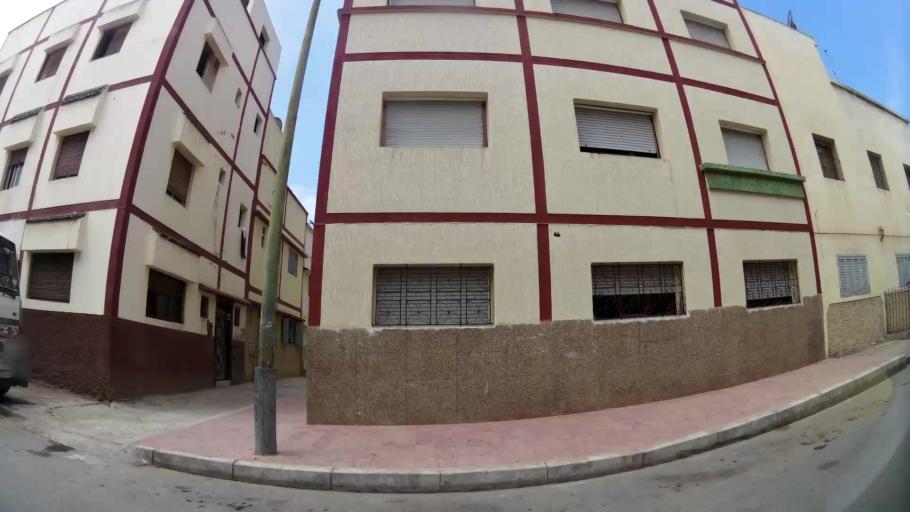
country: MA
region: Rabat-Sale-Zemmour-Zaer
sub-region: Skhirate-Temara
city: Temara
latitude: 33.9831
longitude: -6.8904
